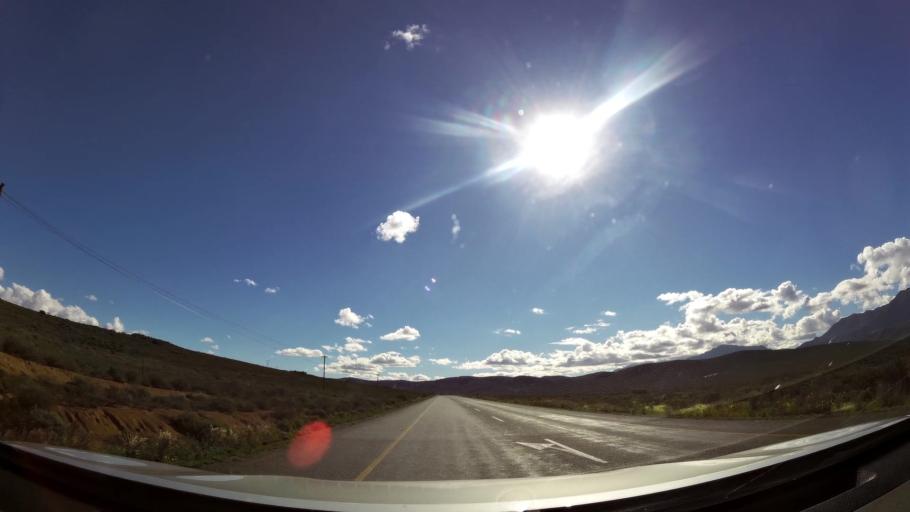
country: ZA
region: Western Cape
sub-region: Cape Winelands District Municipality
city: Worcester
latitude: -33.7453
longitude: 19.7001
